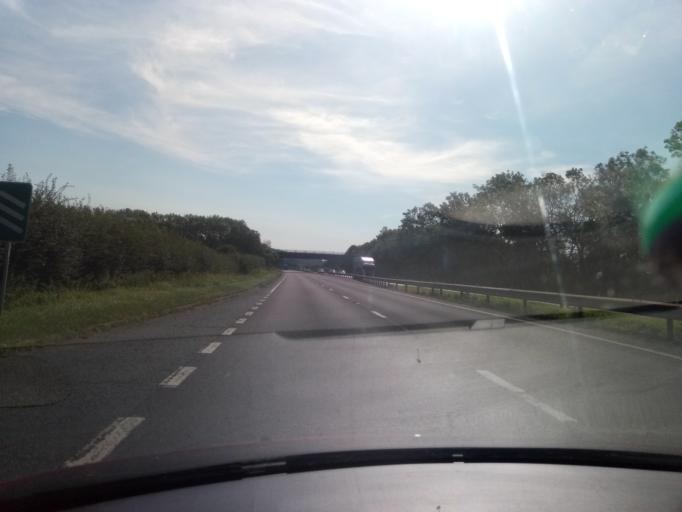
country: GB
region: England
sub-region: North Yorkshire
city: Northallerton
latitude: 54.3843
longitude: -1.3192
